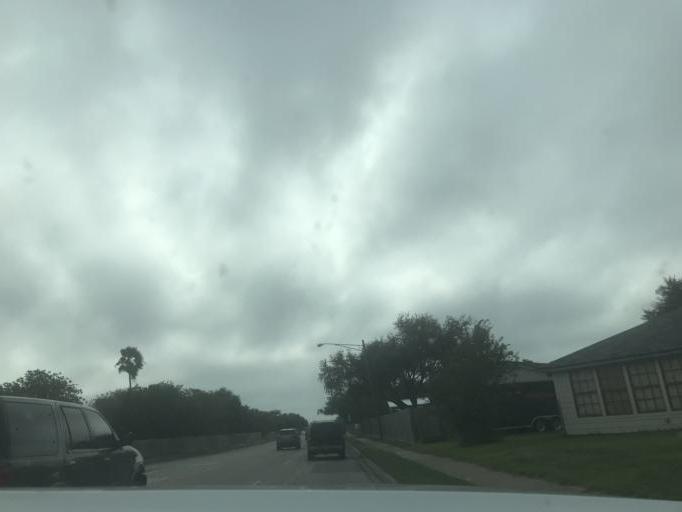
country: US
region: Texas
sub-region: Nueces County
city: Corpus Christi
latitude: 27.6847
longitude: -97.3658
